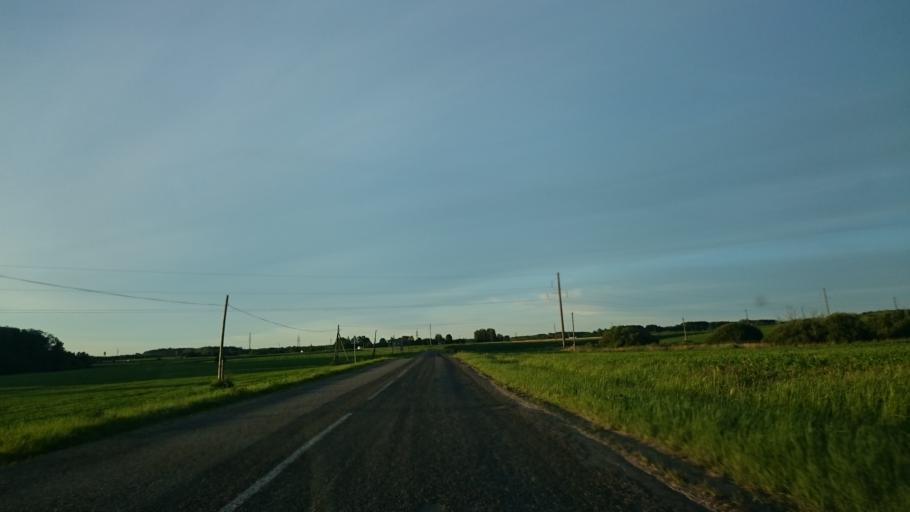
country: LV
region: Saldus Rajons
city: Saldus
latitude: 56.6803
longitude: 22.4992
